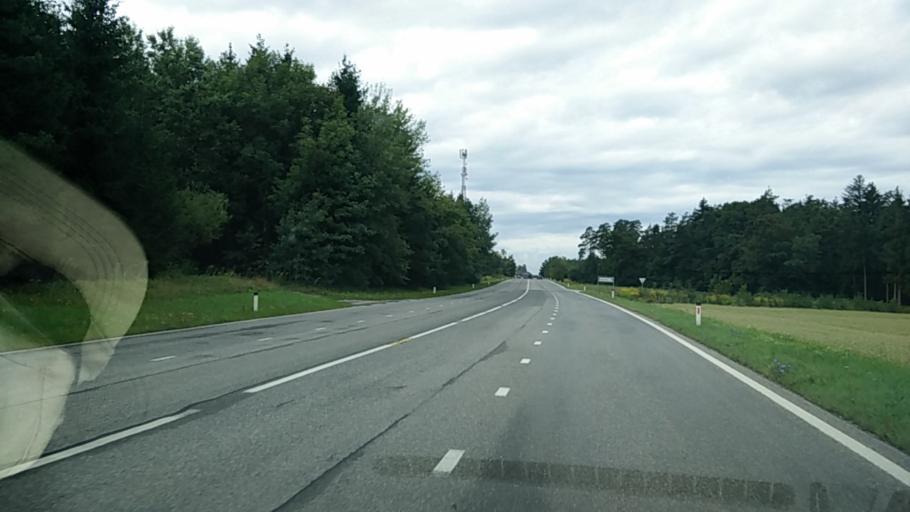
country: AT
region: Carinthia
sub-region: Politischer Bezirk Klagenfurt Land
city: Poggersdorf
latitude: 46.6412
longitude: 14.4367
